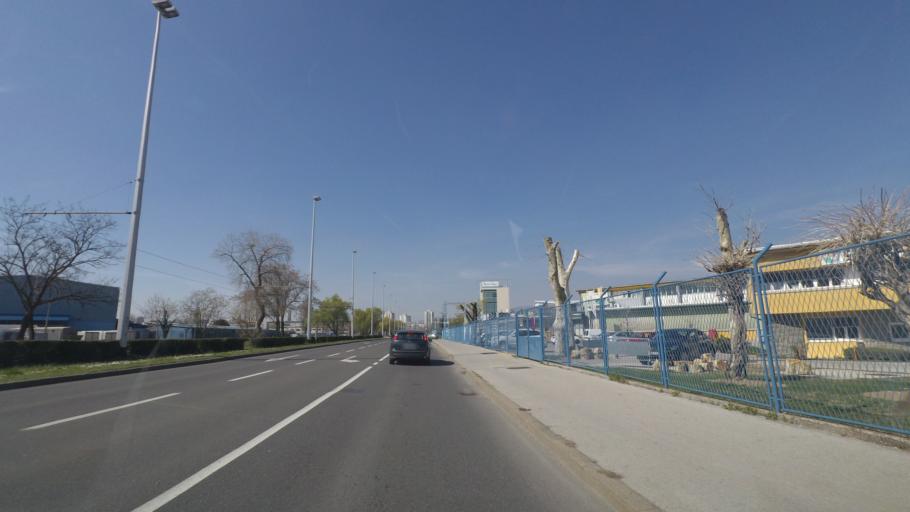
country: HR
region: Grad Zagreb
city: Dubrava
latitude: 45.7999
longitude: 16.0331
